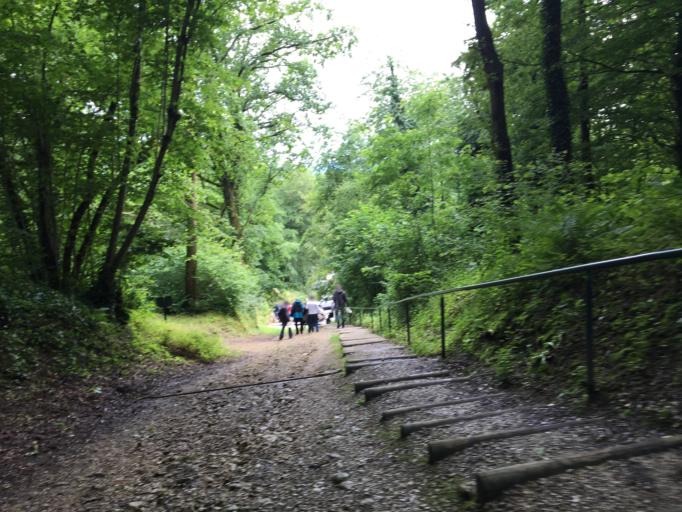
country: FR
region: Lorraine
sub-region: Departement de la Meuse
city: Clermont-en-Argonne
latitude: 49.2046
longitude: 5.0686
